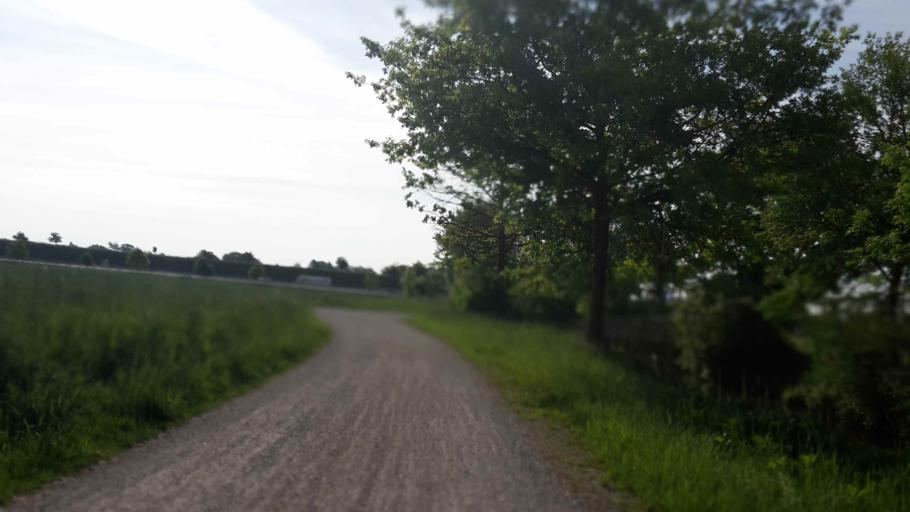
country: DE
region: Bavaria
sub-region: Upper Bavaria
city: Garching bei Munchen
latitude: 48.2394
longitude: 11.6343
